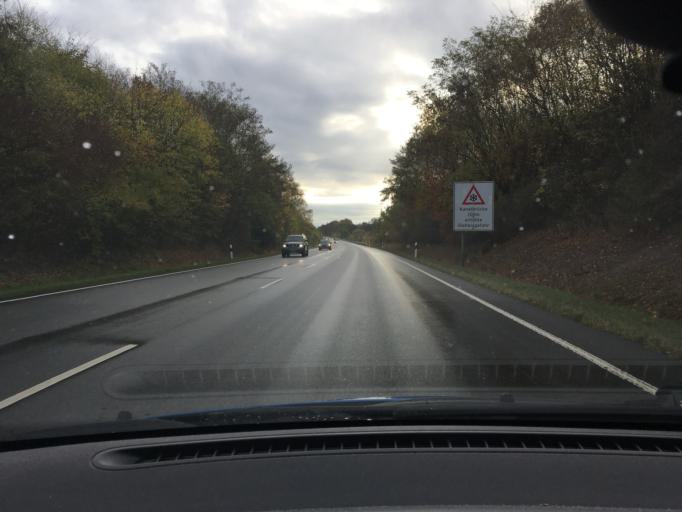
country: DE
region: Schleswig-Holstein
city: Molln
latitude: 53.6325
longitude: 10.6743
